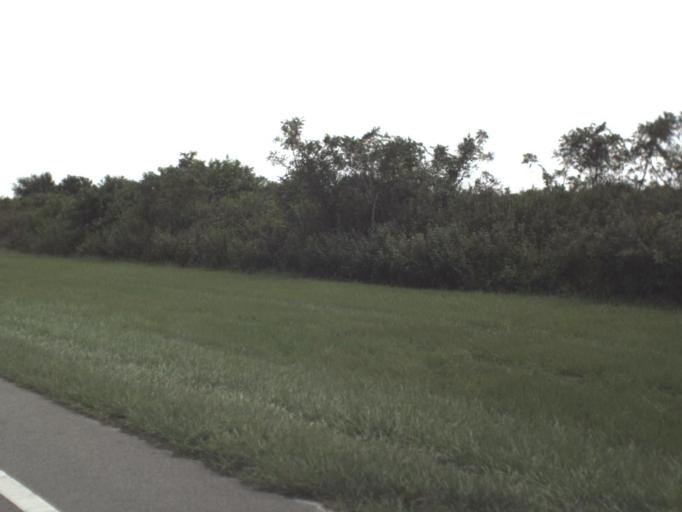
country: US
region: Florida
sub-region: Hillsborough County
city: Wimauma
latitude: 27.5971
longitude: -82.2802
